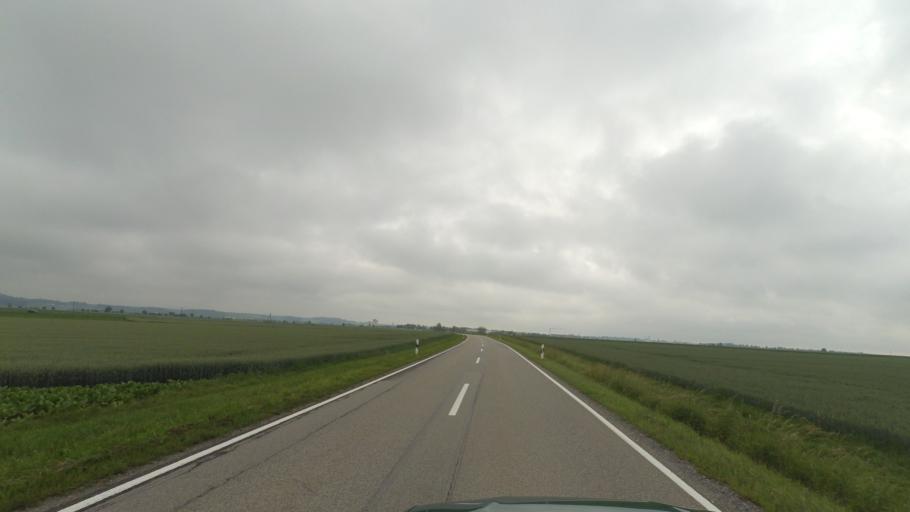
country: DE
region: Bavaria
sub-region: Lower Bavaria
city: Geiselhoring
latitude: 48.8054
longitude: 12.3846
